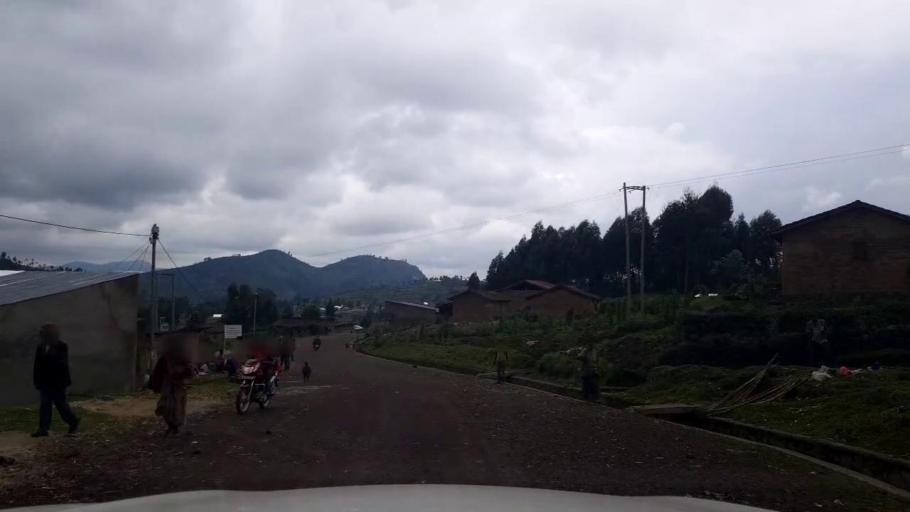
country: RW
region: Northern Province
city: Musanze
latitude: -1.5750
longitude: 29.4903
